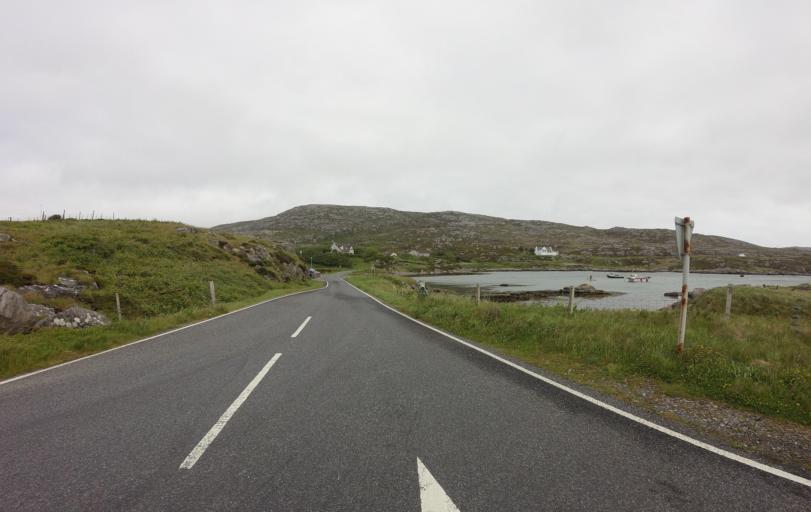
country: GB
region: Scotland
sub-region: Eilean Siar
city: Isle of South Uist
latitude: 57.1040
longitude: -7.3267
